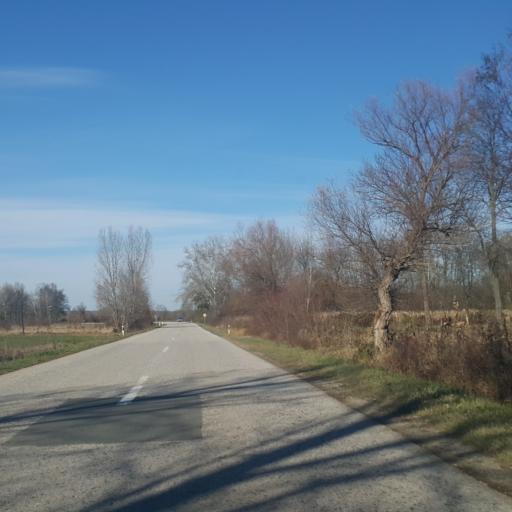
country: RS
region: Central Serbia
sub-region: Sumadijski Okrug
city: Topola
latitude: 44.2509
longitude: 20.8295
